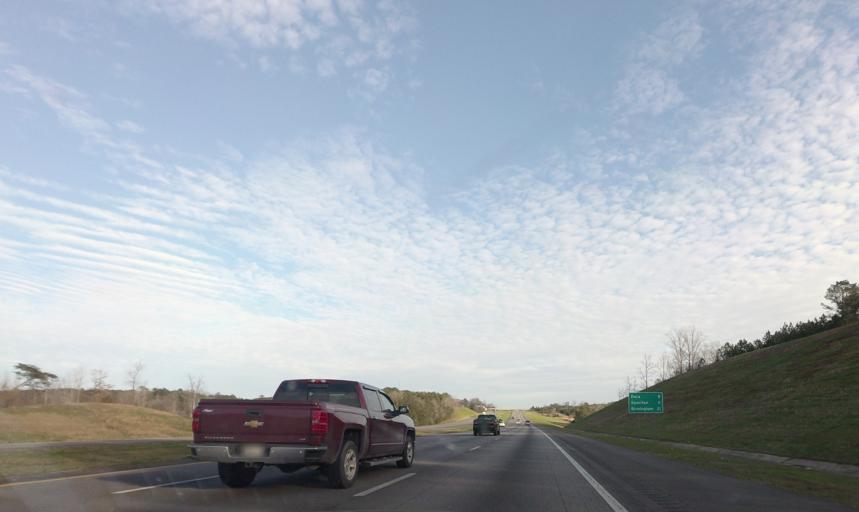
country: US
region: Alabama
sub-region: Walker County
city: Cordova
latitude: 33.7157
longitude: -87.1676
